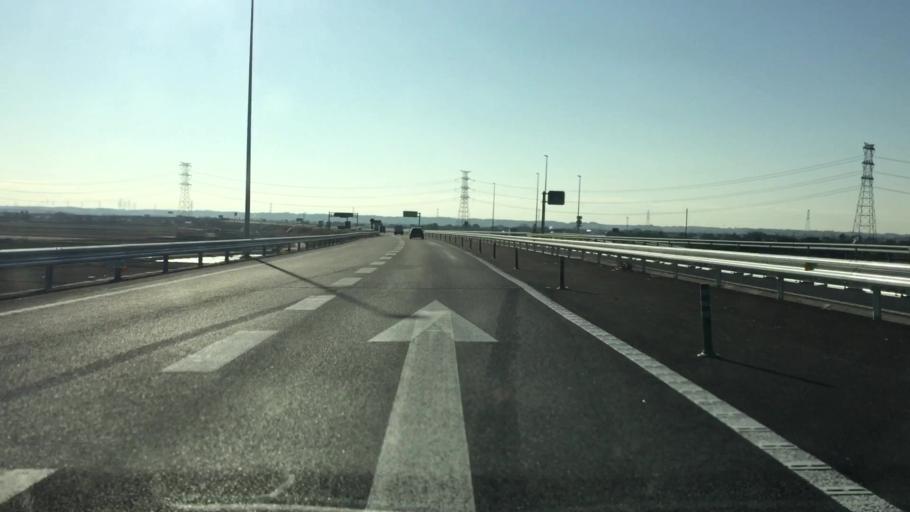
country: JP
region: Ibaraki
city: Inashiki
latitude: 35.9239
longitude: 140.3477
